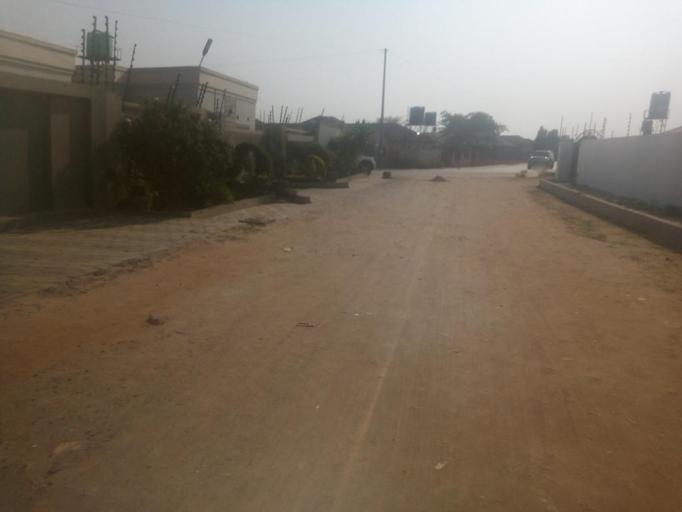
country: ZM
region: Lusaka
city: Lusaka
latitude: -15.3994
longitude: 28.3906
